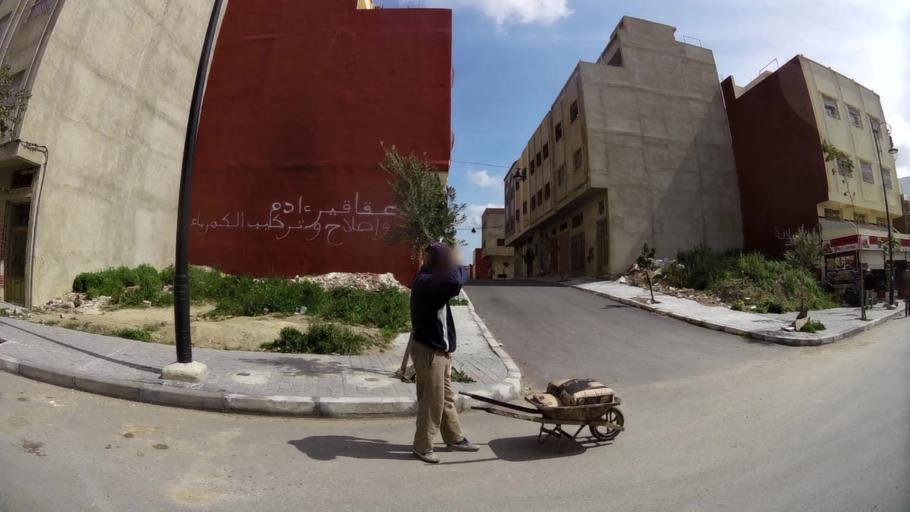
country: MA
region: Tanger-Tetouan
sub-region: Tanger-Assilah
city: Tangier
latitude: 35.7616
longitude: -5.7608
